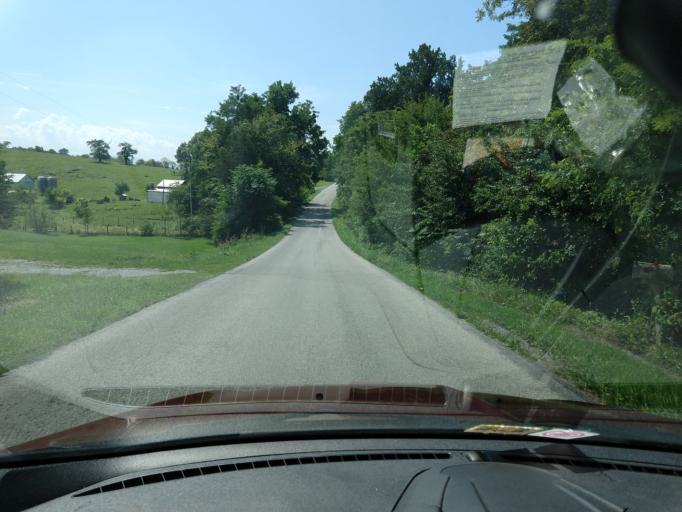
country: US
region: Virginia
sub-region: Rockingham County
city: Broadway
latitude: 38.5691
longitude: -78.8873
